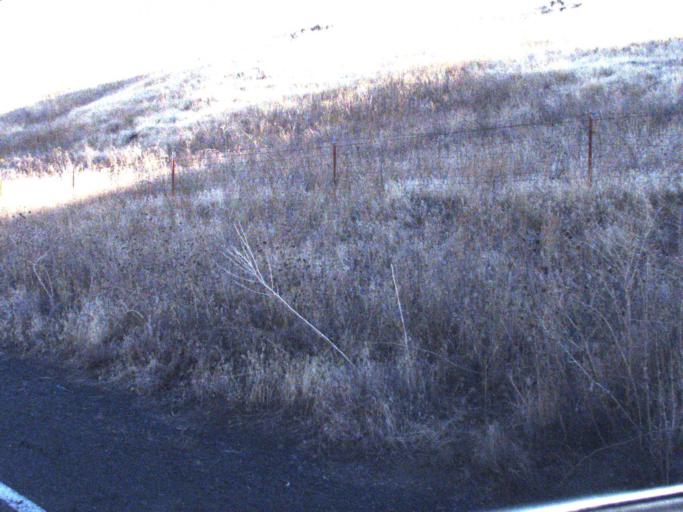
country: US
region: Washington
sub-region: Walla Walla County
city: Waitsburg
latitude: 46.6699
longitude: -118.3113
